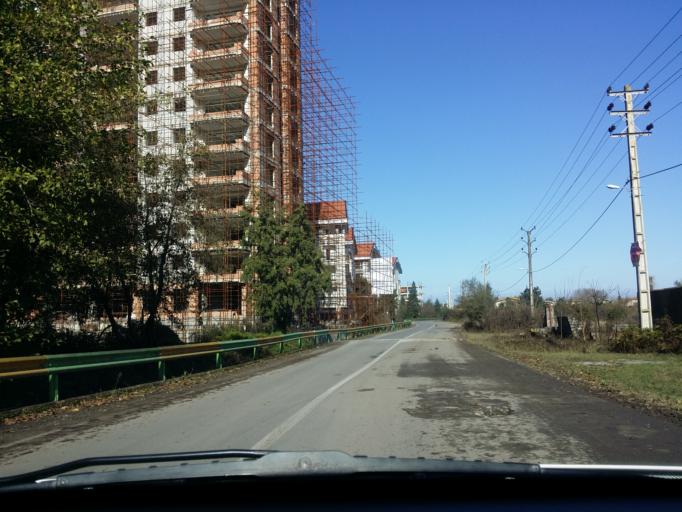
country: IR
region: Mazandaran
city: Chalus
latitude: 36.6775
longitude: 51.3146
